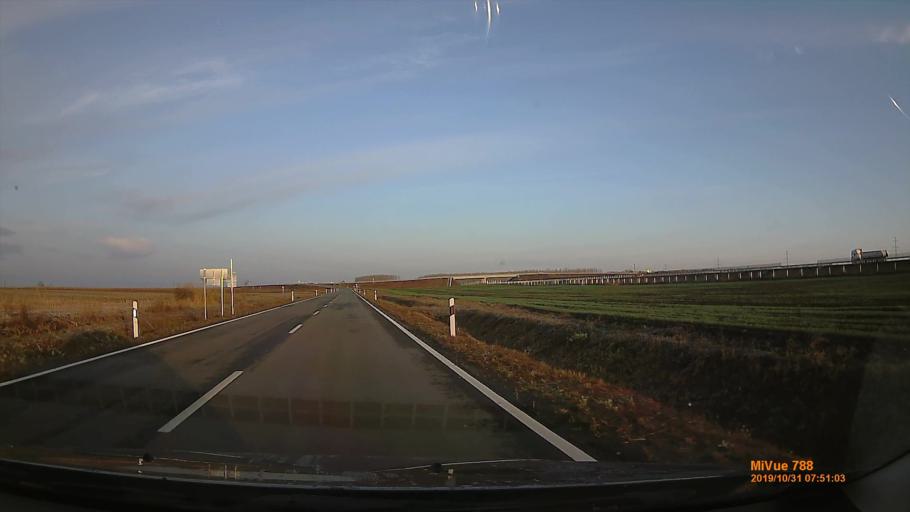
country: HU
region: Pest
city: Pilis
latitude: 47.3065
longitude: 19.5591
